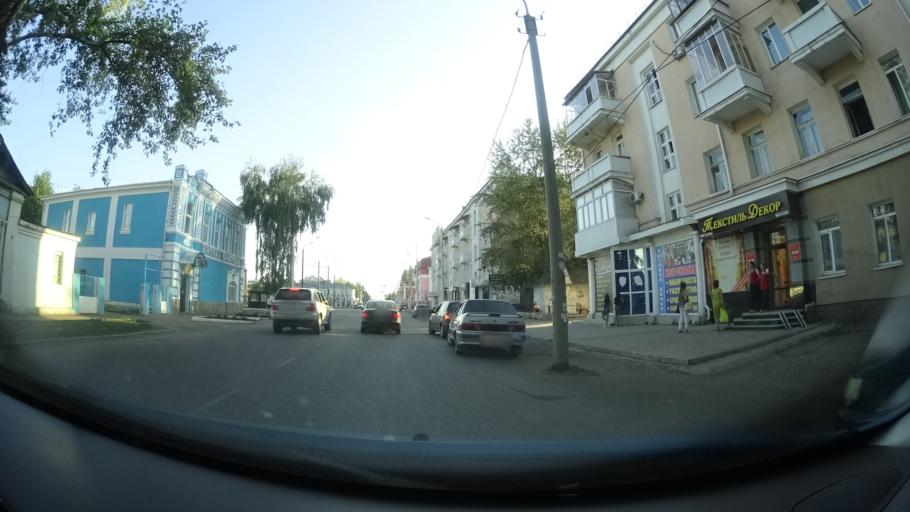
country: RU
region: Bashkortostan
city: Sterlitamak
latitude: 53.6202
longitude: 55.9623
